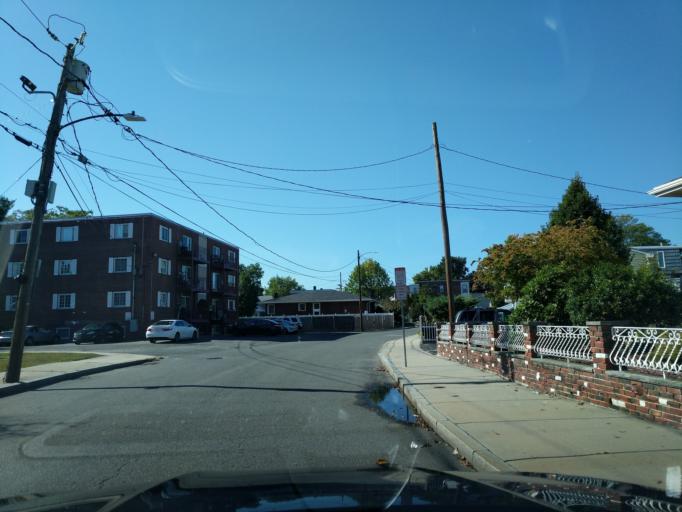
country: US
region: Massachusetts
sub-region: Suffolk County
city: Chelsea
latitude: 42.4098
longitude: -71.0308
